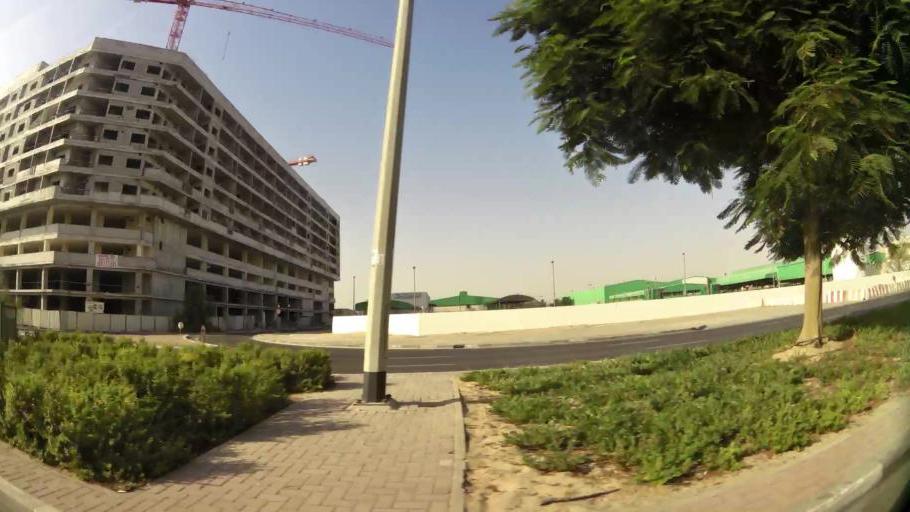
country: AE
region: Ash Shariqah
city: Sharjah
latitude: 25.2796
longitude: 55.3814
